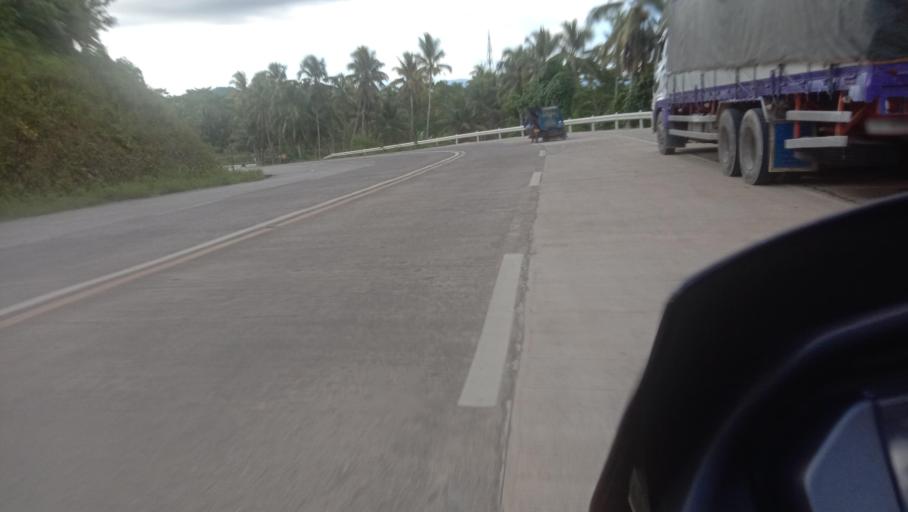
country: PH
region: Caraga
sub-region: Province of Surigao del Sur
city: Barobo
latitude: 8.5231
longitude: 126.1202
